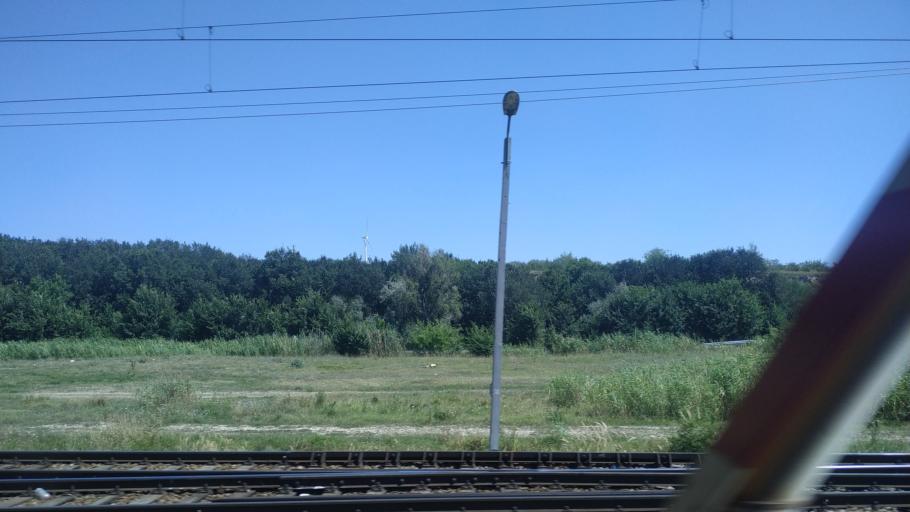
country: RO
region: Constanta
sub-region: Comuna Saligny
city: Saligny
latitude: 44.2853
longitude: 28.0792
